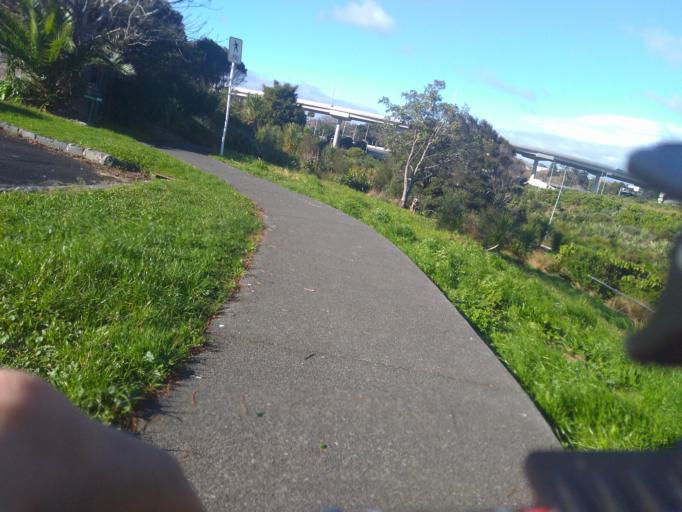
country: NZ
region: Auckland
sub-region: Auckland
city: Rosebank
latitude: -36.8701
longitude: 174.7036
